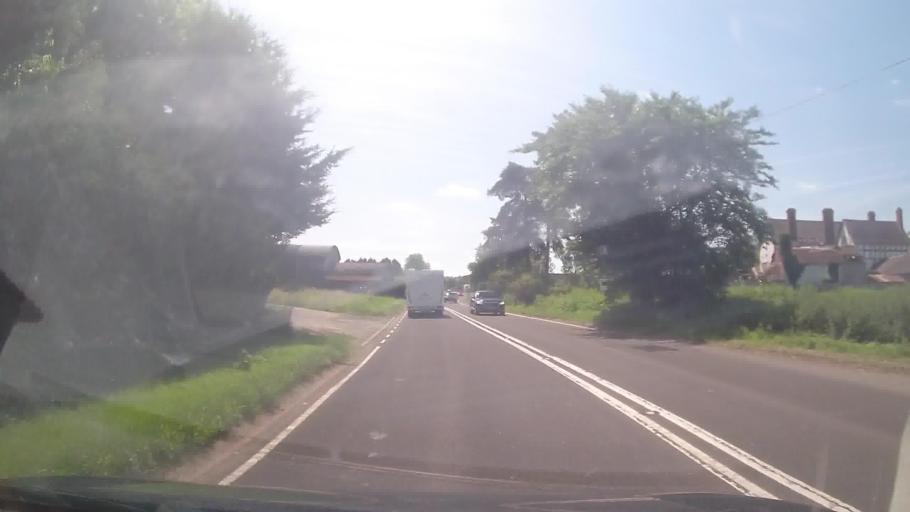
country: GB
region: England
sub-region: Herefordshire
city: Orleton
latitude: 52.3146
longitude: -2.7070
